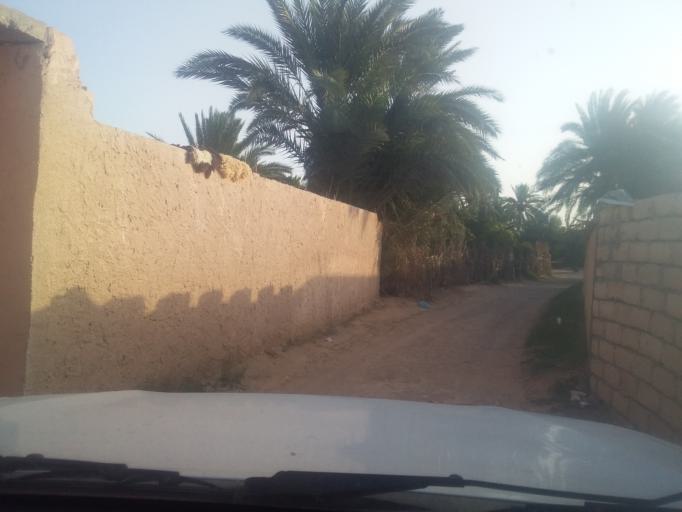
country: TN
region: Qabis
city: Gabes
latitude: 33.6291
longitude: 10.2958
